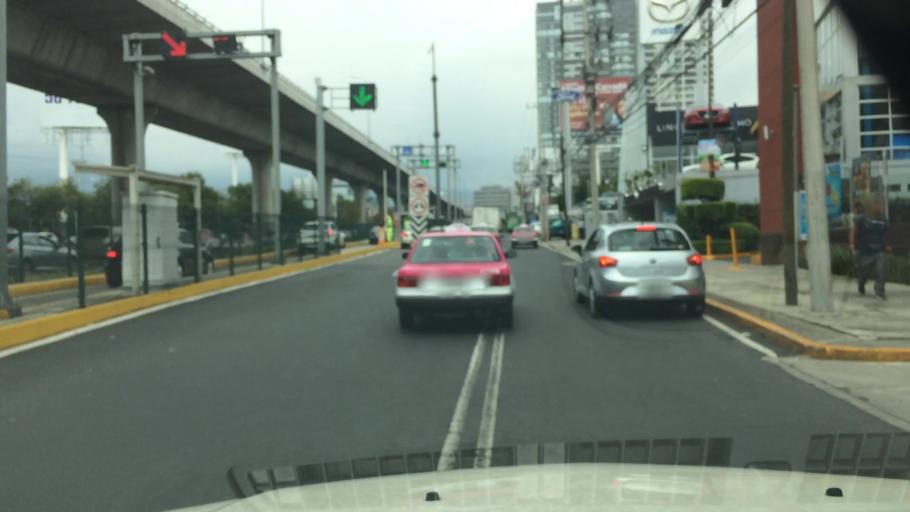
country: MX
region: Mexico City
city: Magdalena Contreras
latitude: 19.3068
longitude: -99.2110
